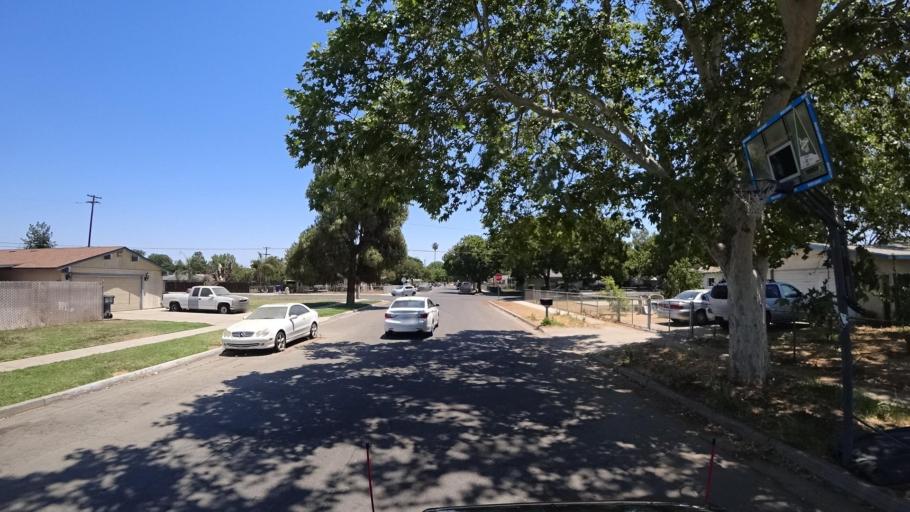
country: US
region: California
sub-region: Fresno County
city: West Park
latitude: 36.7240
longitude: -119.8227
